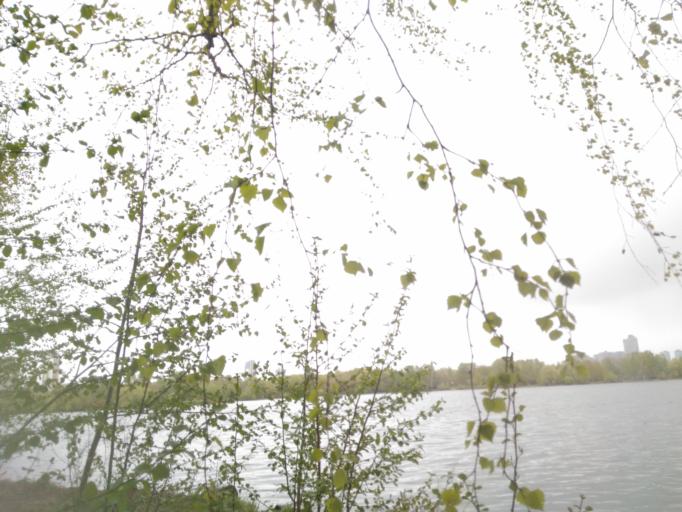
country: RU
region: Moscow
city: Strogino
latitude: 55.7897
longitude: 37.4174
